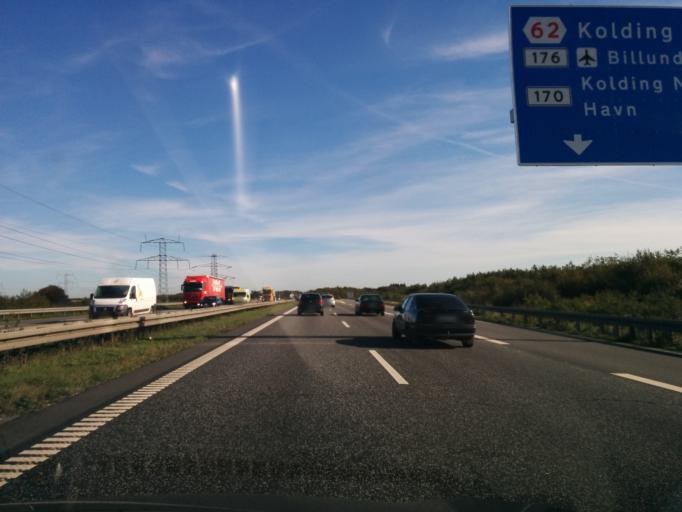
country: DK
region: South Denmark
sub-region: Kolding Kommune
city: Kolding
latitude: 55.5312
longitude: 9.4860
